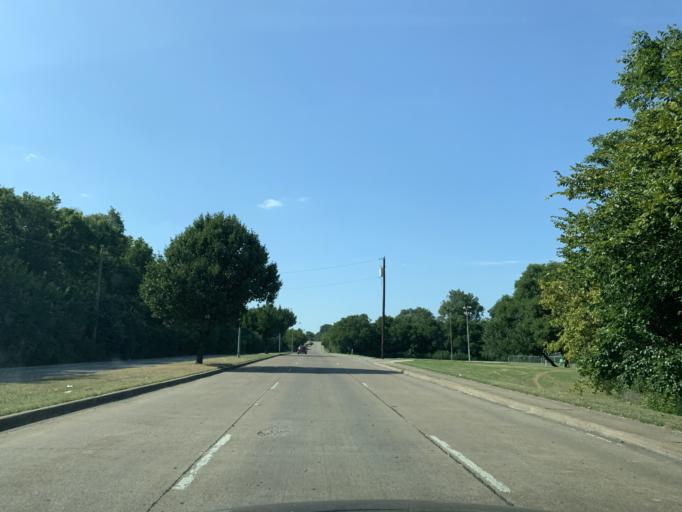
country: US
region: Texas
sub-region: Dallas County
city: Hutchins
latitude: 32.6845
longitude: -96.7684
